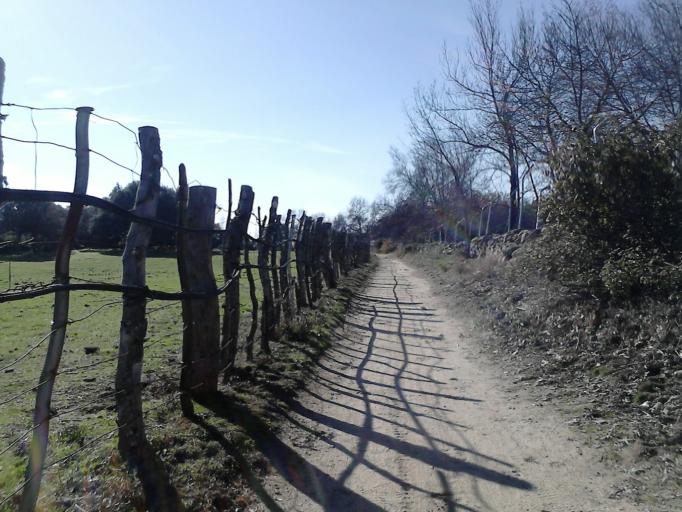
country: ES
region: Madrid
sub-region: Provincia de Madrid
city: El Escorial
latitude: 40.6073
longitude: -4.0930
